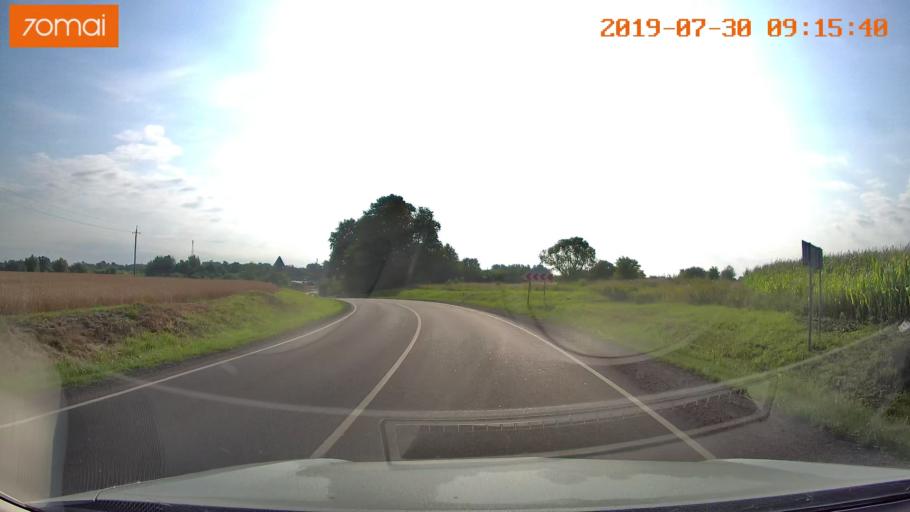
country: RU
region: Kaliningrad
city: Nesterov
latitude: 54.6332
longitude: 22.5447
